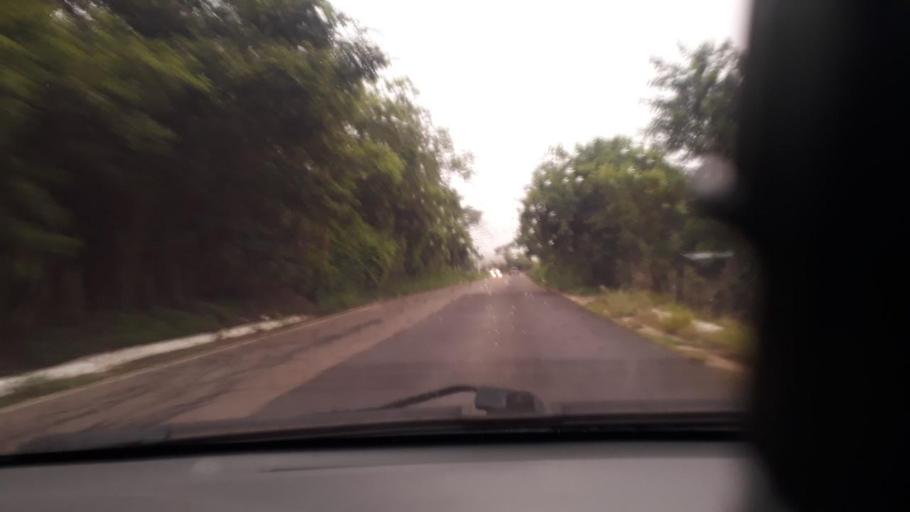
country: GT
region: Jutiapa
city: Jalpatagua
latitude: 14.1778
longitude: -90.0444
